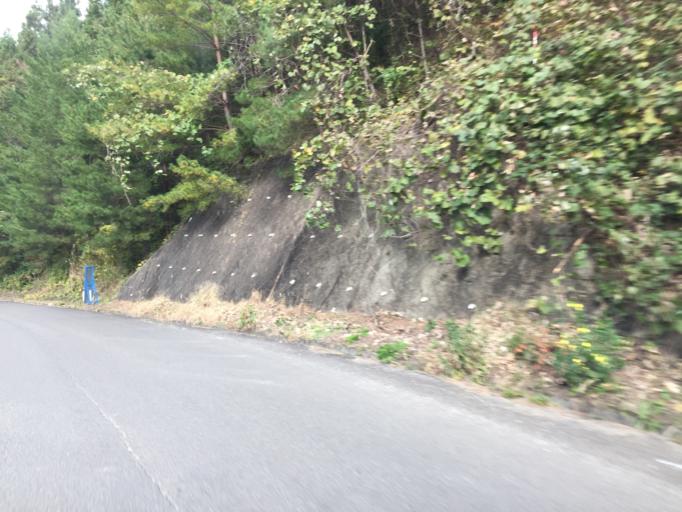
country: JP
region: Miyagi
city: Marumori
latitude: 37.8110
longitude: 140.7398
